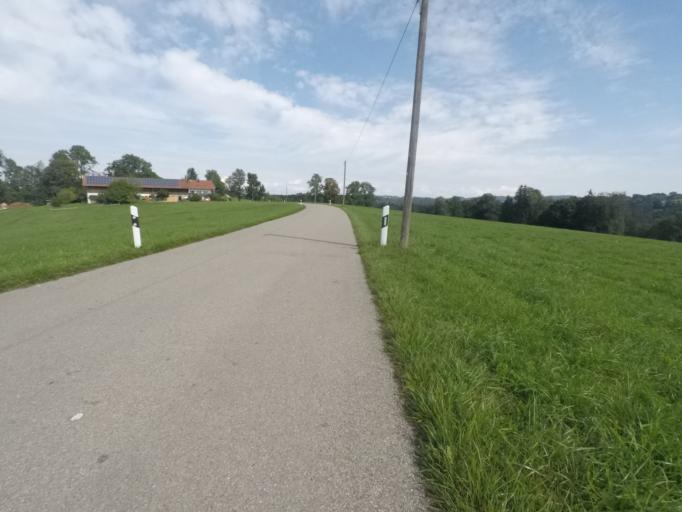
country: DE
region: Bavaria
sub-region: Upper Bavaria
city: Kreut
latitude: 47.7979
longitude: 11.5148
